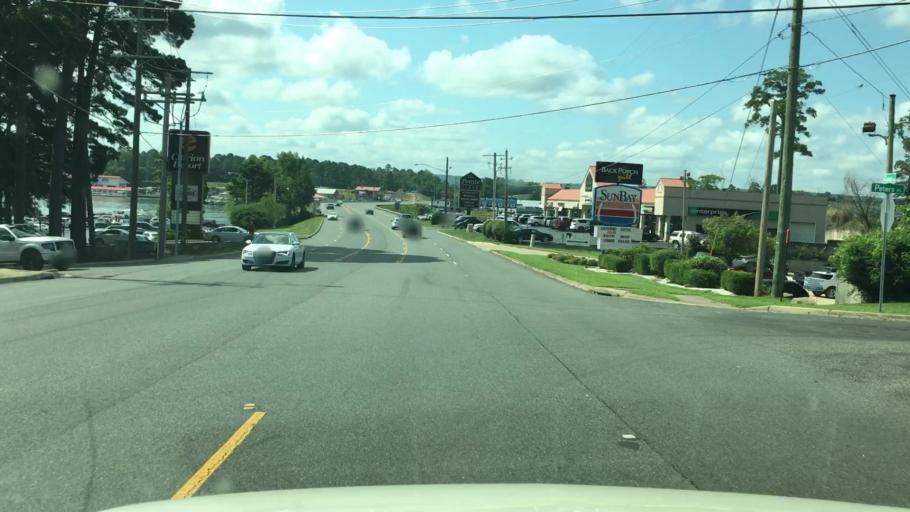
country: US
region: Arkansas
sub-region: Garland County
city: Lake Hamilton
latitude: 34.4442
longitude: -93.0899
